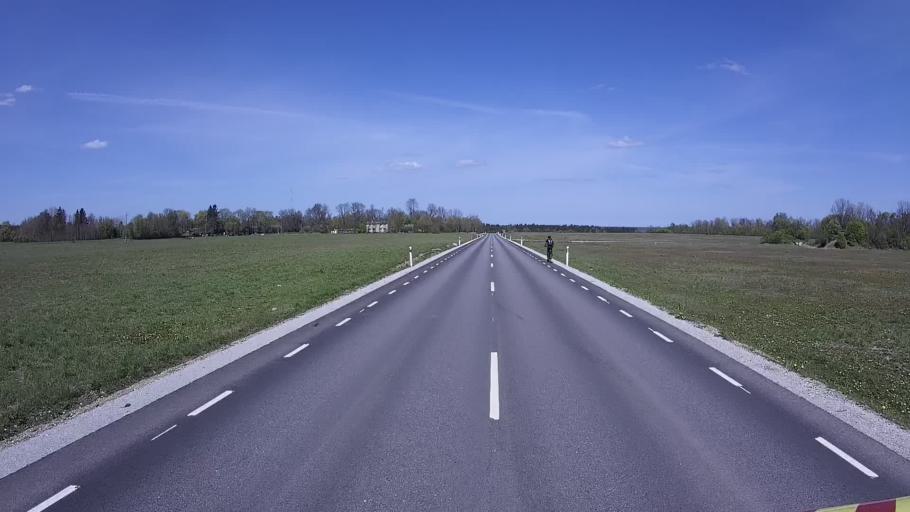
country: EE
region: Harju
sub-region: Paldiski linn
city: Paldiski
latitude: 59.2065
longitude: 24.0956
